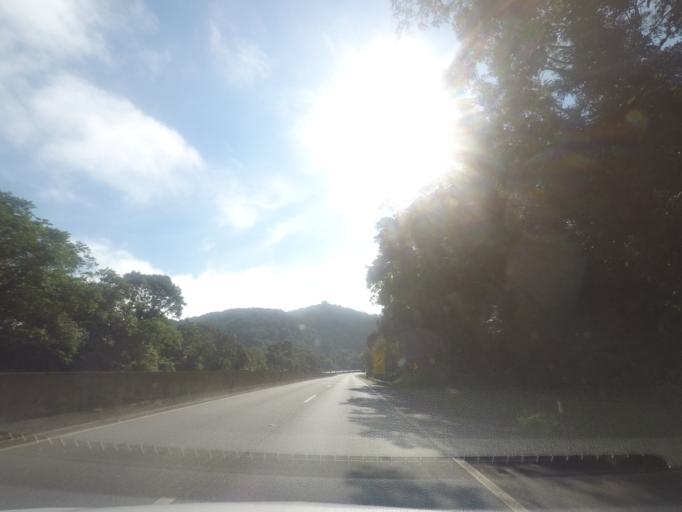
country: BR
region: Parana
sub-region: Piraquara
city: Piraquara
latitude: -25.5933
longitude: -48.8961
